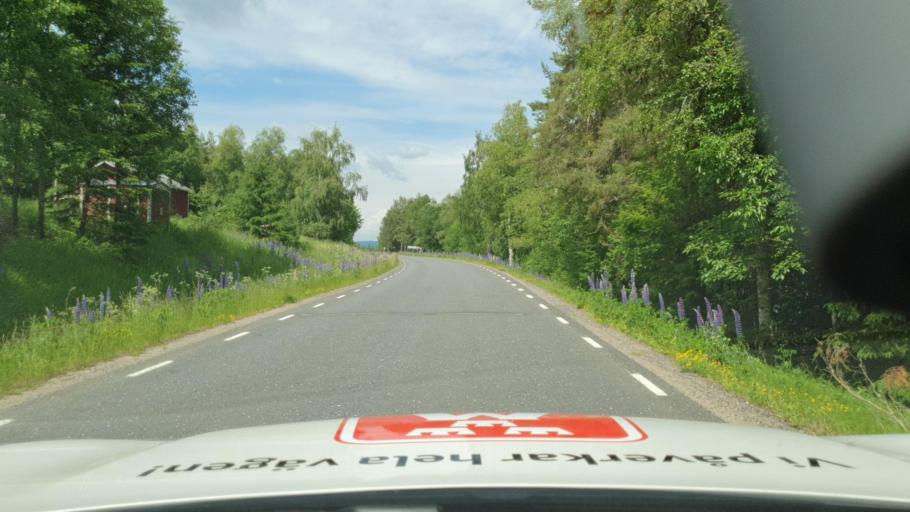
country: SE
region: Vaermland
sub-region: Torsby Kommun
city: Torsby
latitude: 60.6565
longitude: 12.7037
